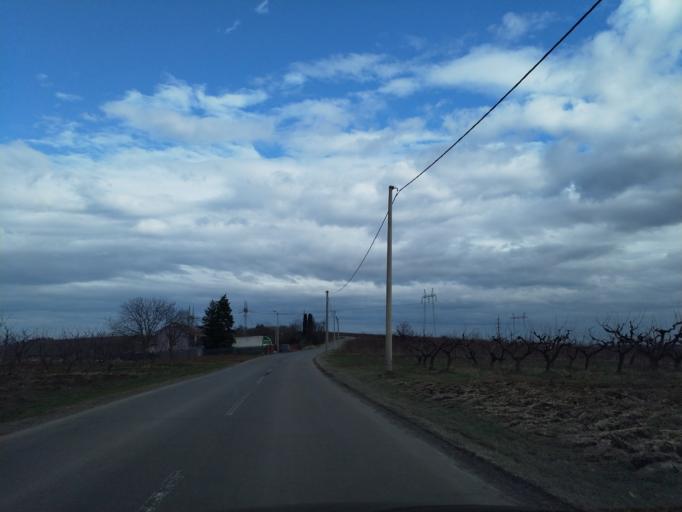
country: RS
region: Central Serbia
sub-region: Belgrade
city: Grocka
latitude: 44.6288
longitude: 20.7455
